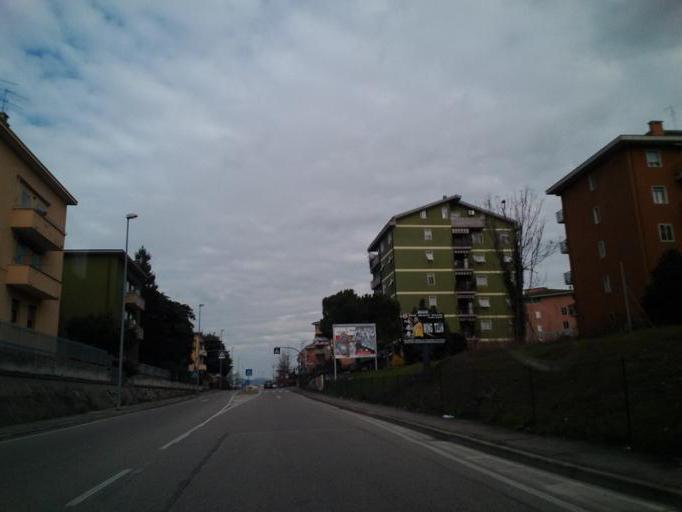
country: IT
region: Veneto
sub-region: Provincia di Verona
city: Verona
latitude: 45.4212
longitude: 10.9631
